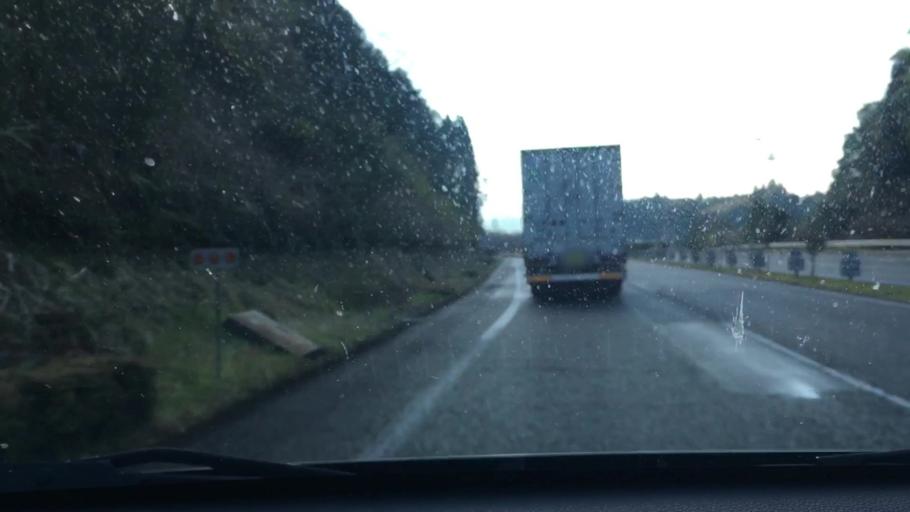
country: JP
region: Kagoshima
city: Okuchi-shinohara
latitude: 31.9456
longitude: 130.7249
